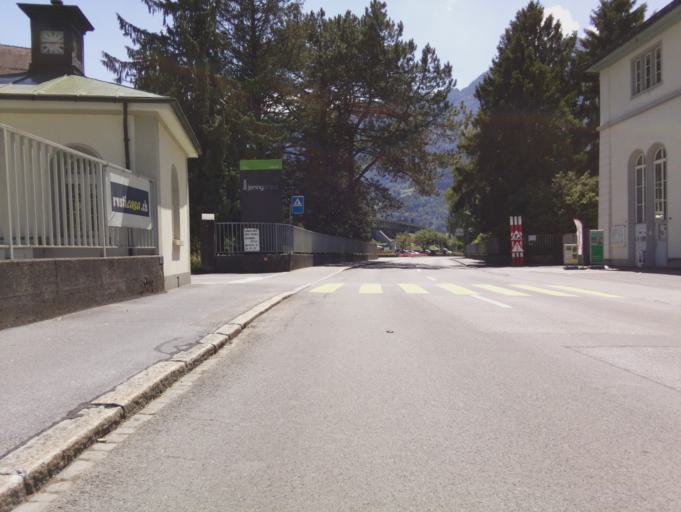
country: CH
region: Glarus
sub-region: Glarus
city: Niederurnen
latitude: 47.1331
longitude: 9.0609
